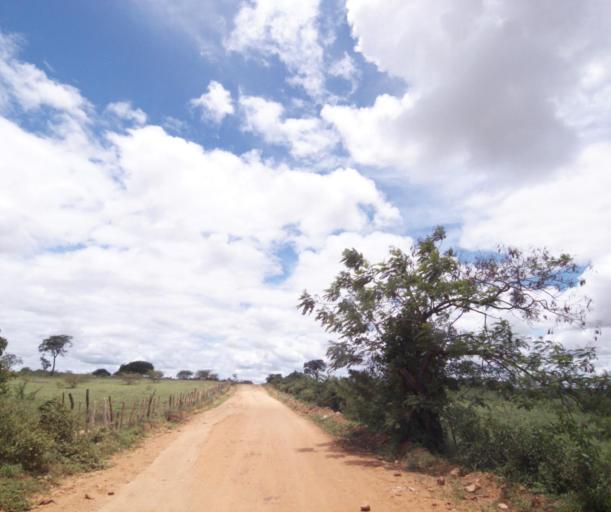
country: BR
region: Bahia
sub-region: Tanhacu
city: Tanhacu
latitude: -14.1549
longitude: -41.1967
